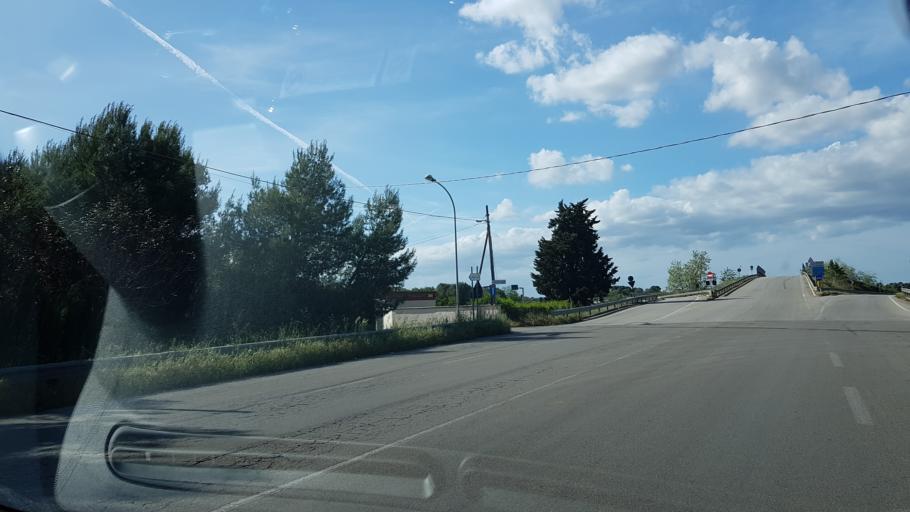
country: IT
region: Apulia
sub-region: Provincia di Brindisi
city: Mesagne
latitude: 40.5658
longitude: 17.7864
